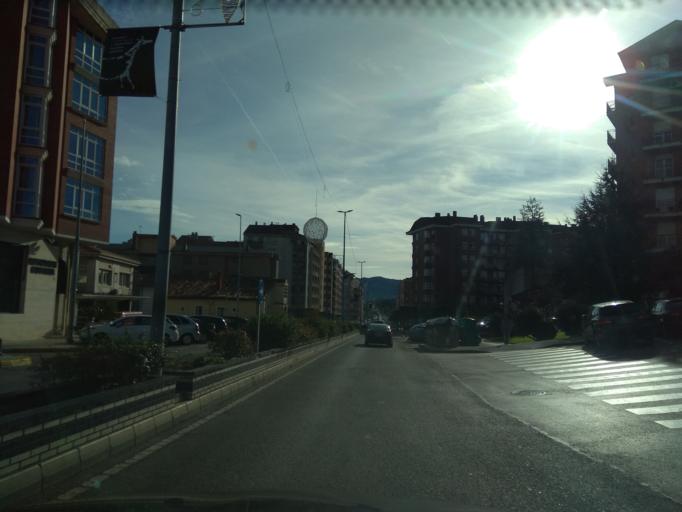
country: ES
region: Cantabria
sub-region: Provincia de Cantabria
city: El Astillero
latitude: 43.4199
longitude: -3.8464
